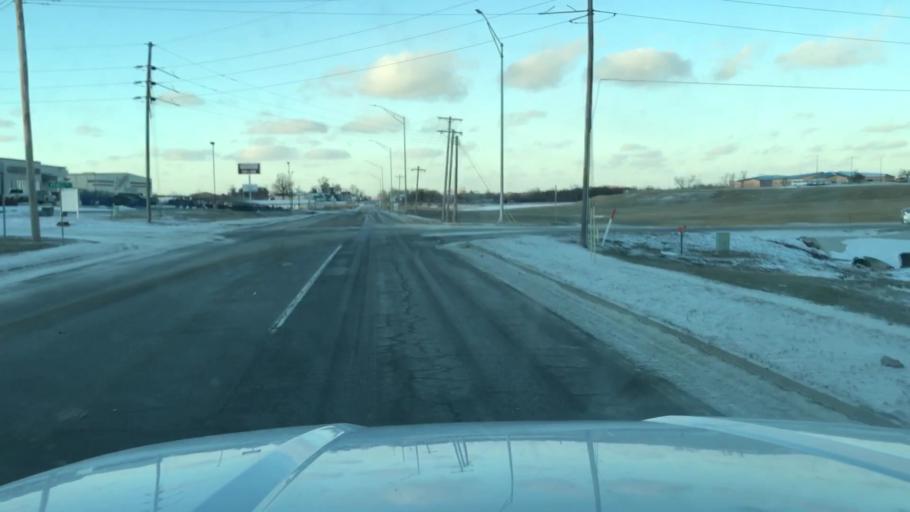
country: US
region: Missouri
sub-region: Clinton County
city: Cameron
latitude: 39.7603
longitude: -94.2343
